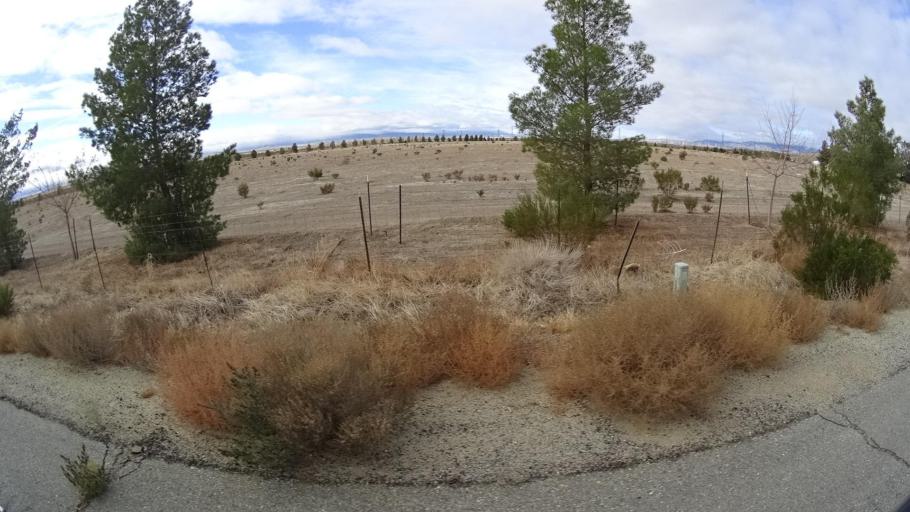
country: US
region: California
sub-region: Kern County
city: Rosamond
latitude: 34.8767
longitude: -118.2919
